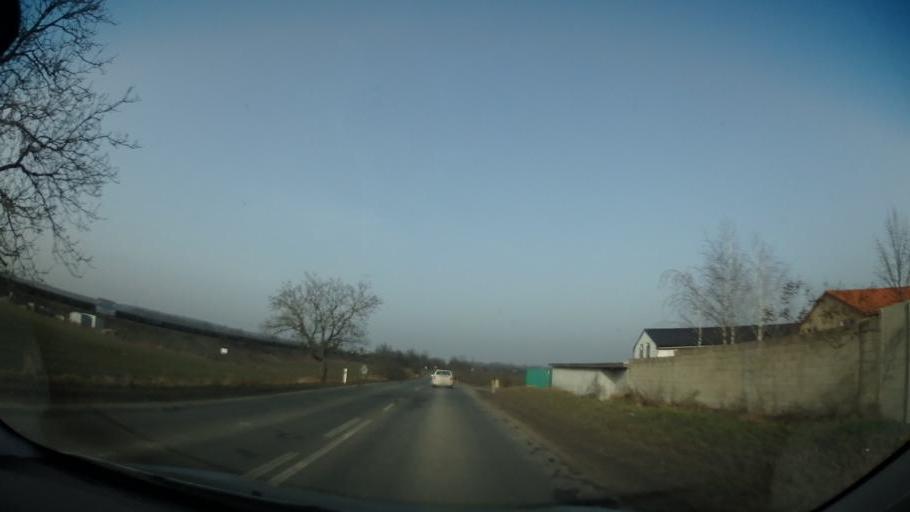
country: CZ
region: South Moravian
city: Rajhrad
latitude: 49.0908
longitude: 16.5940
